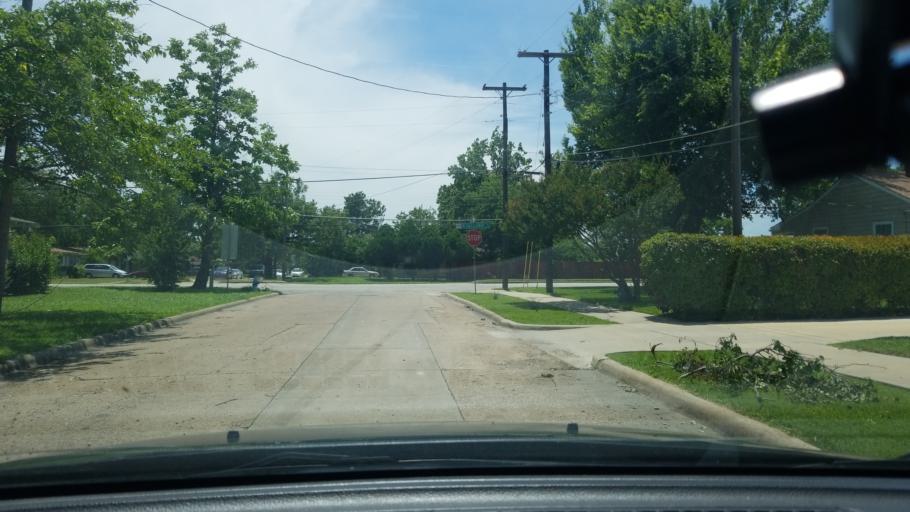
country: US
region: Texas
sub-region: Dallas County
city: Mesquite
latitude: 32.7902
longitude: -96.6090
